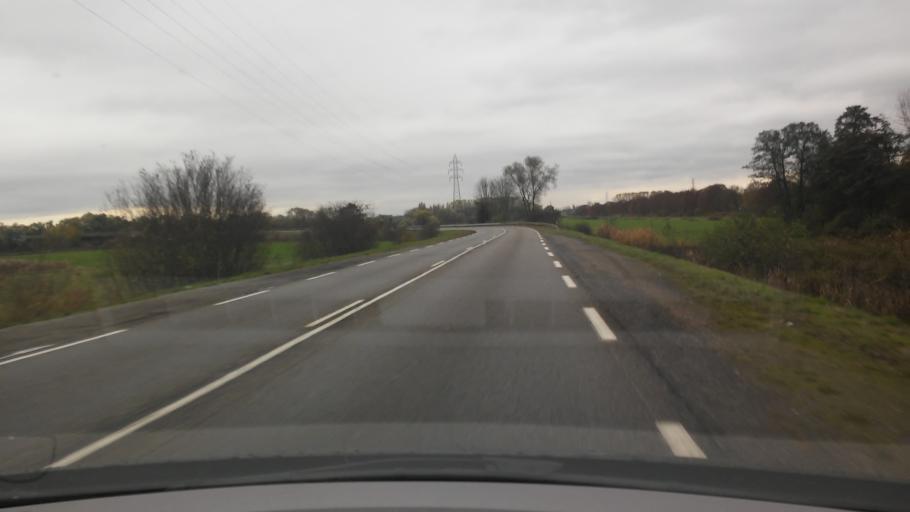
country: FR
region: Lorraine
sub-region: Departement de la Moselle
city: Mondelange
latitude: 49.2588
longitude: 6.1821
